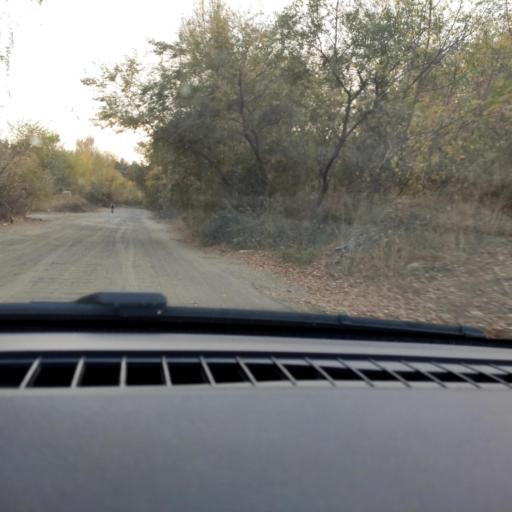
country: RU
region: Voronezj
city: Pridonskoy
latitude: 51.6766
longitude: 39.1262
